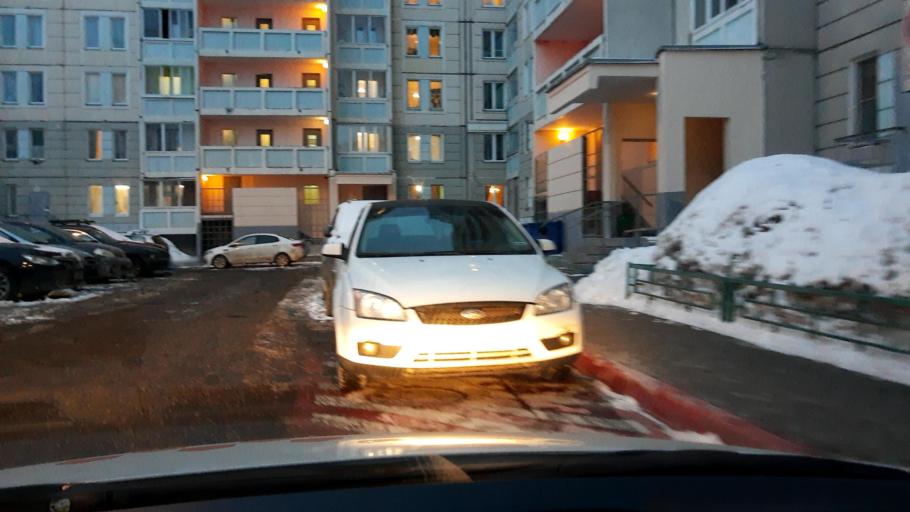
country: RU
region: Moskovskaya
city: Kommunarka
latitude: 55.5406
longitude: 37.5213
